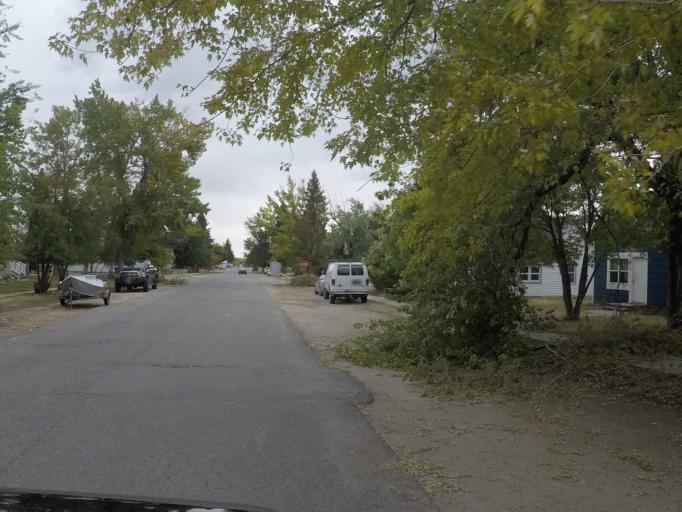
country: US
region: Montana
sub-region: Carbon County
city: Red Lodge
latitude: 45.1893
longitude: -109.2445
